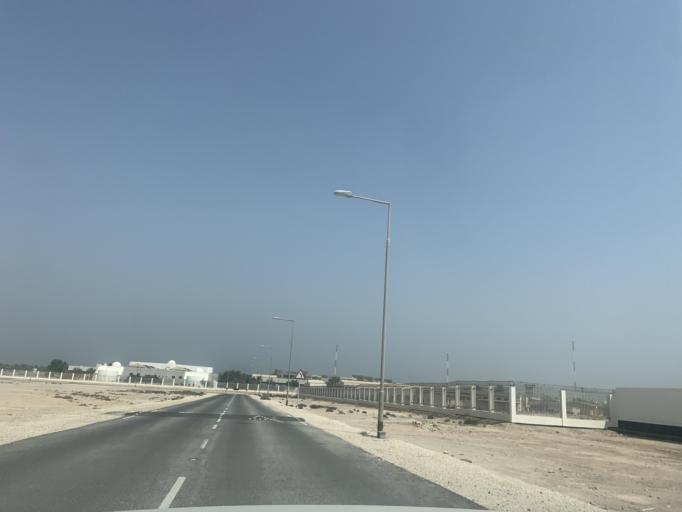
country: BH
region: Central Governorate
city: Madinat Hamad
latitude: 26.1563
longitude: 50.4740
